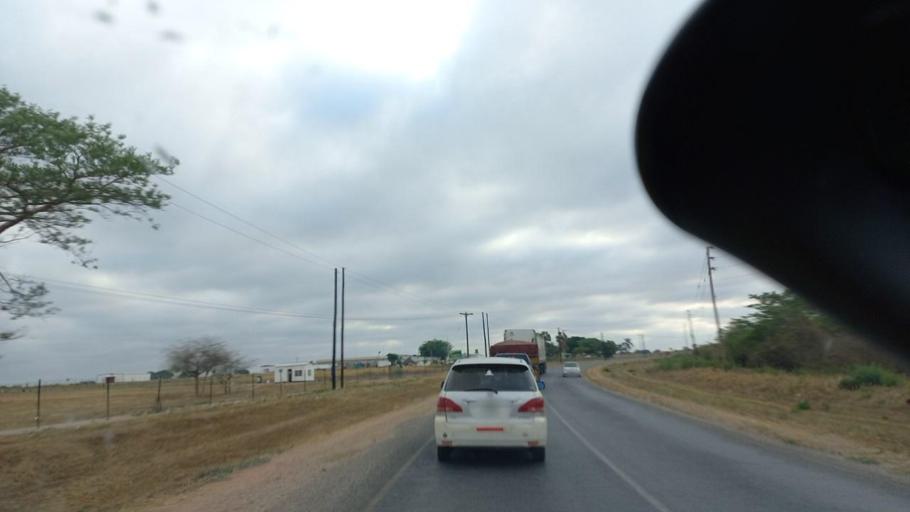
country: ZM
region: Lusaka
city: Chongwe
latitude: -15.3422
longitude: 28.5188
